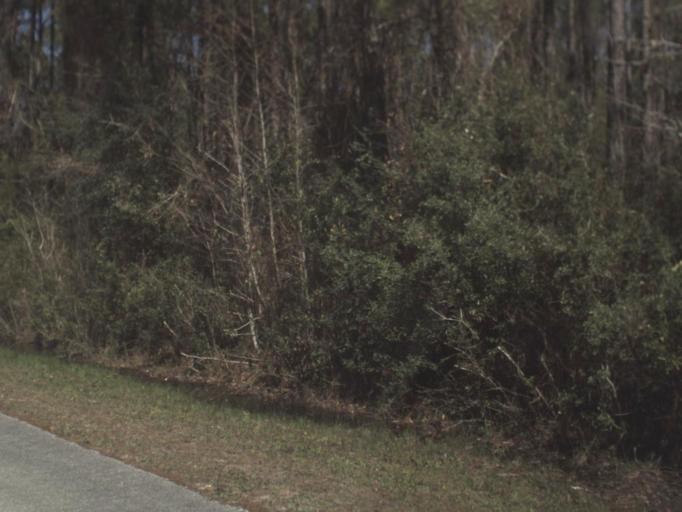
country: US
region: Florida
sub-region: Leon County
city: Woodville
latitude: 30.1862
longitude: -84.2141
